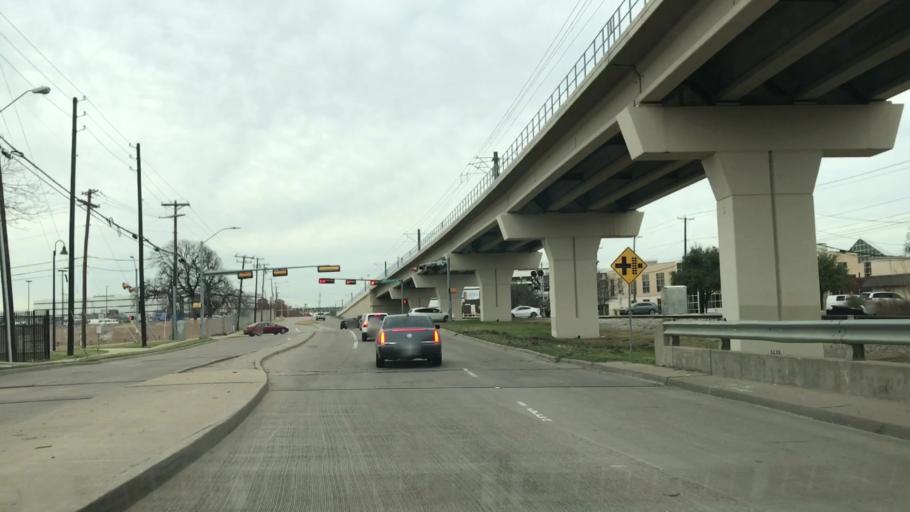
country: US
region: Texas
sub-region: Dallas County
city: University Park
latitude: 32.8460
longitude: -96.8699
